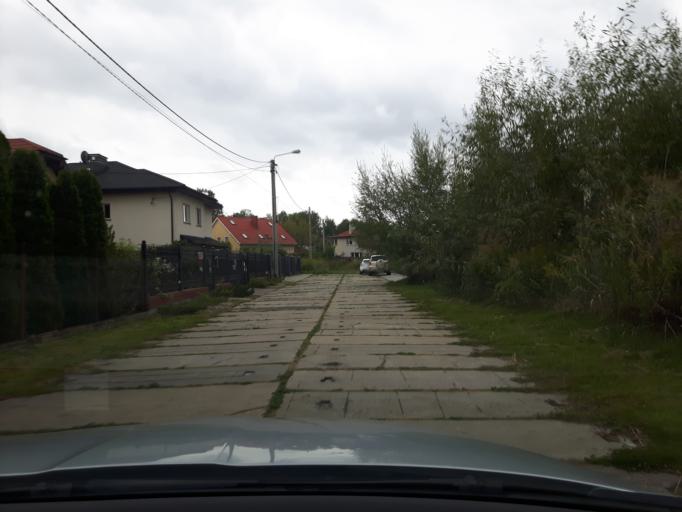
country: PL
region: Masovian Voivodeship
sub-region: Powiat wolominski
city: Kobylka
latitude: 52.3351
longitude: 21.1886
